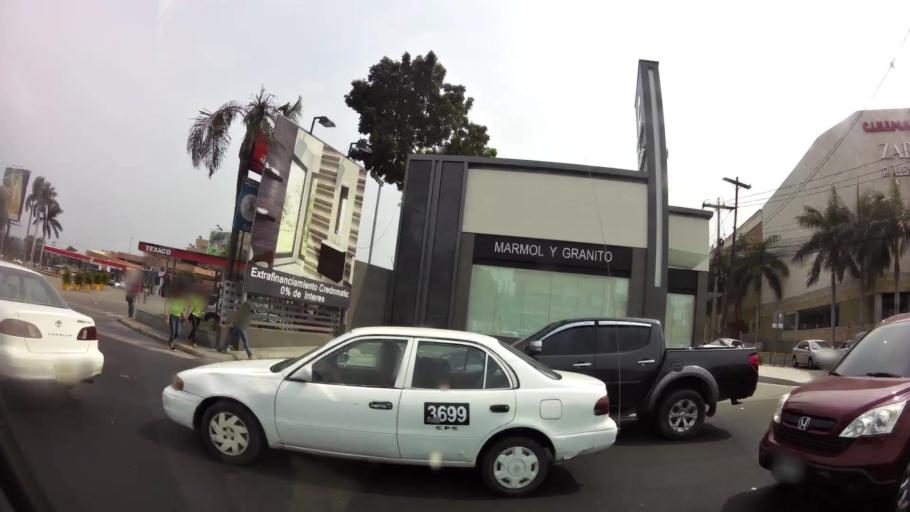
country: HN
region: Cortes
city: San Pedro Sula
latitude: 15.4969
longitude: -88.0348
